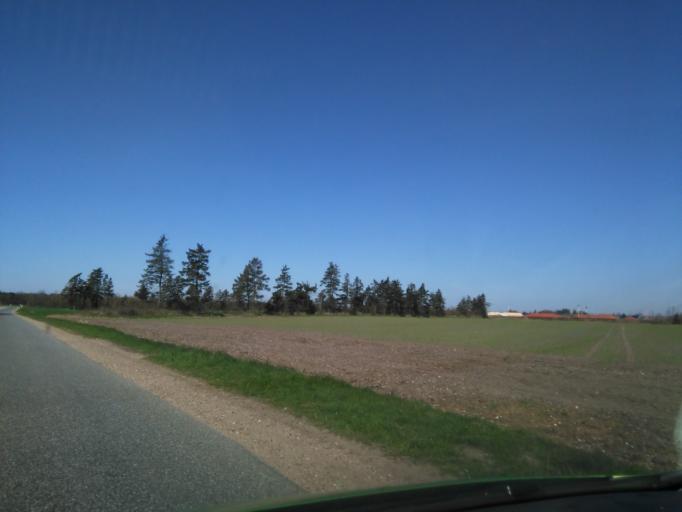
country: DK
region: South Denmark
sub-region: Billund Kommune
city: Billund
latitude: 55.7101
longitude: 9.1118
